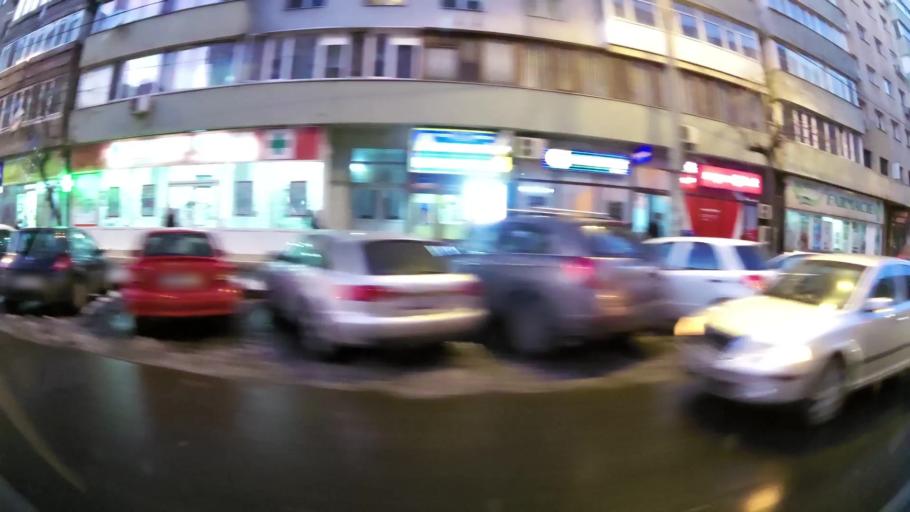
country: RO
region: Ilfov
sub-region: Comuna Fundeni-Dobroesti
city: Fundeni
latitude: 44.4442
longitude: 26.1445
